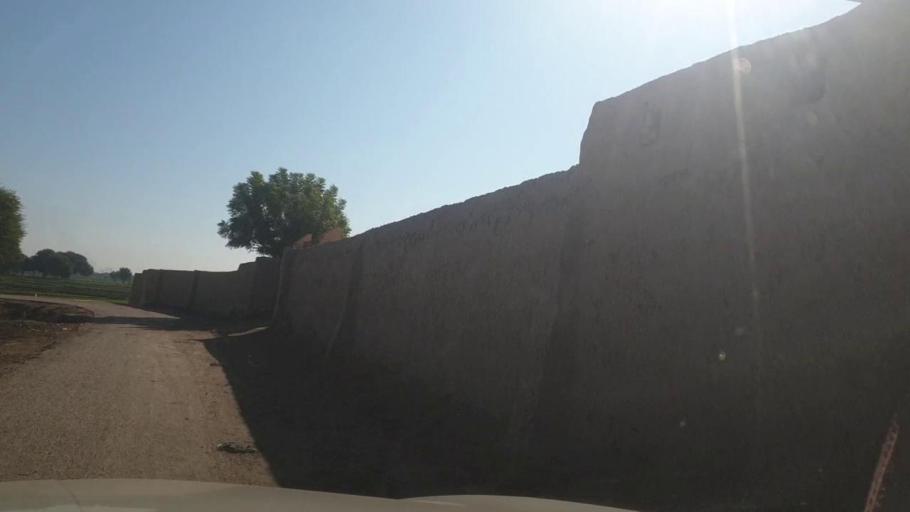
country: PK
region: Sindh
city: Bhan
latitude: 26.5446
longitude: 67.6624
